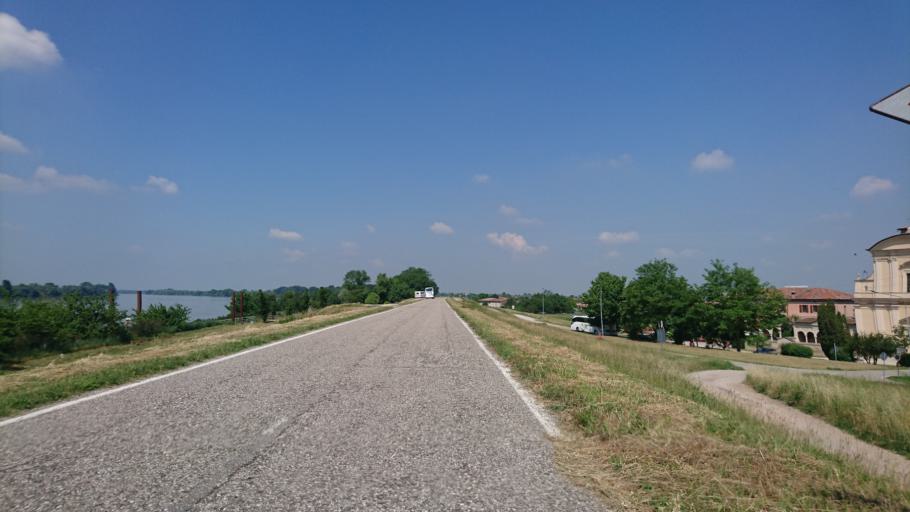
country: IT
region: Lombardy
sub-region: Provincia di Mantova
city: Sustinente
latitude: 45.0682
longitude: 11.0004
